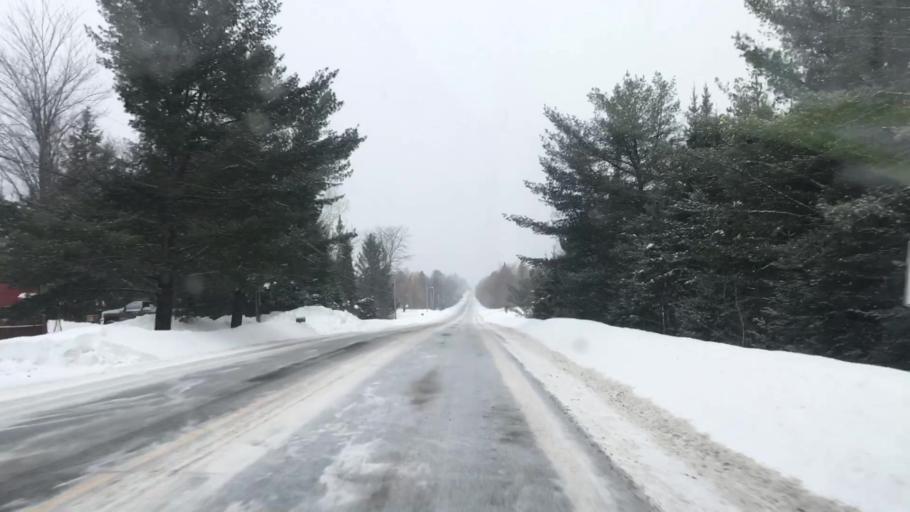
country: US
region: Maine
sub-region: Penobscot County
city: Medway
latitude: 45.5240
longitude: -68.3560
